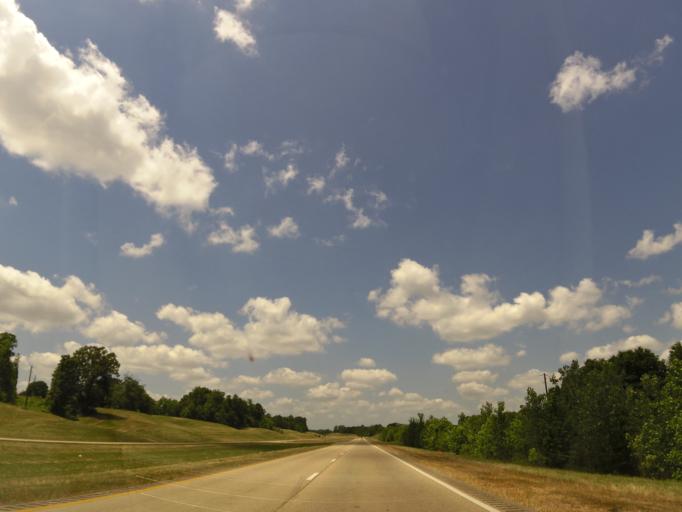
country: US
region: Mississippi
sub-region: Pontotoc County
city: Pontotoc
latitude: 34.2786
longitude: -88.9478
